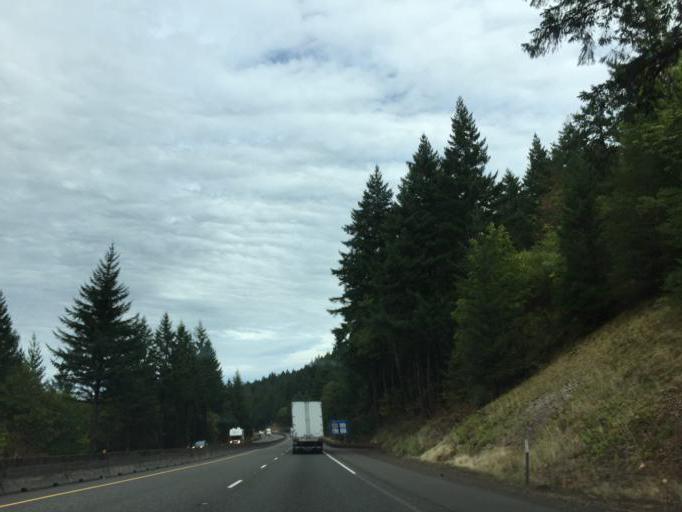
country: US
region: Oregon
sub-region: Hood River County
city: Cascade Locks
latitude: 45.6506
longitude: -121.9094
